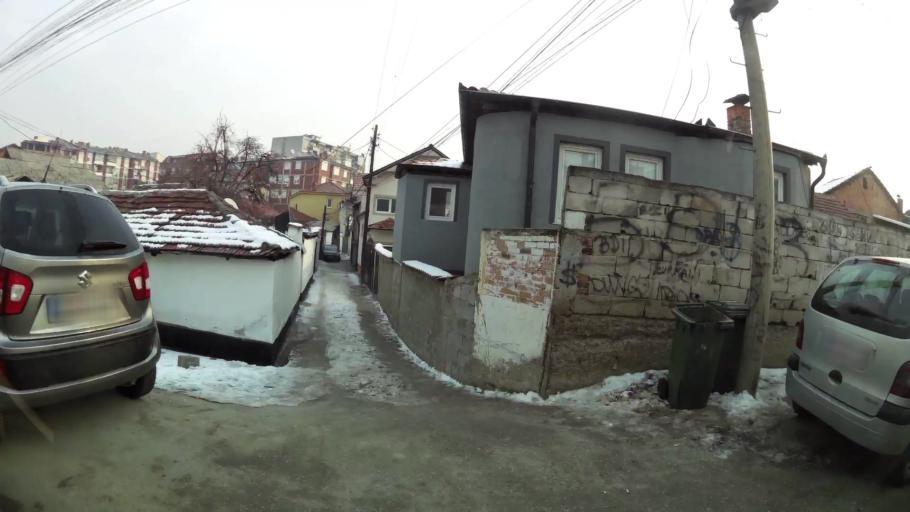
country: MK
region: Cair
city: Cair
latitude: 42.0167
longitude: 21.4388
